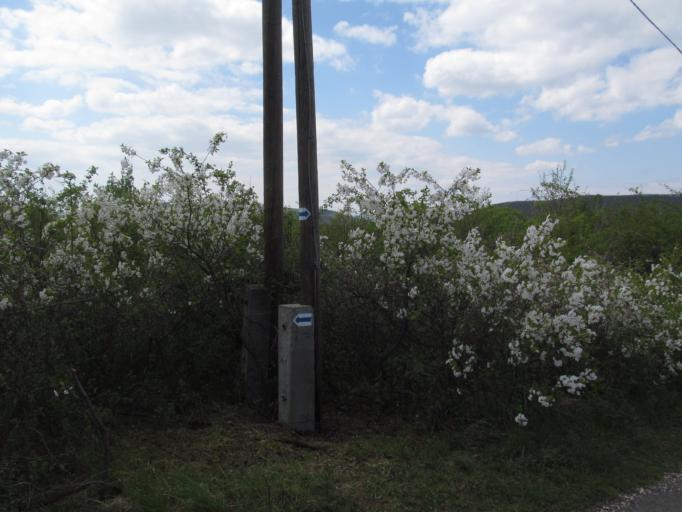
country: HU
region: Veszprem
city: Revfueloep
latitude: 46.8951
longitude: 17.5755
